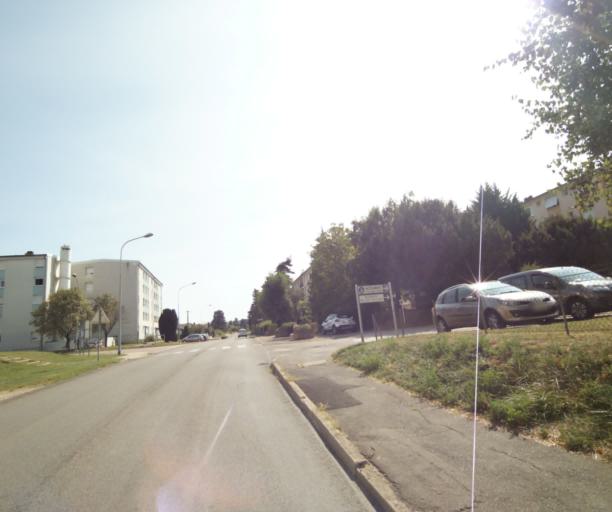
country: FR
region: Bourgogne
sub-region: Departement de Saone-et-Loire
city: Tournus
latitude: 46.5613
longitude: 4.9039
